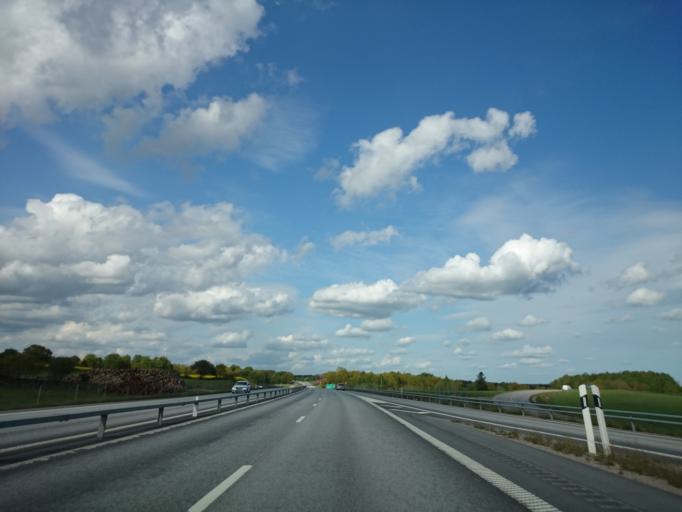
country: SE
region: Skane
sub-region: Horby Kommun
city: Hoerby
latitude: 55.8677
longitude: 13.6973
